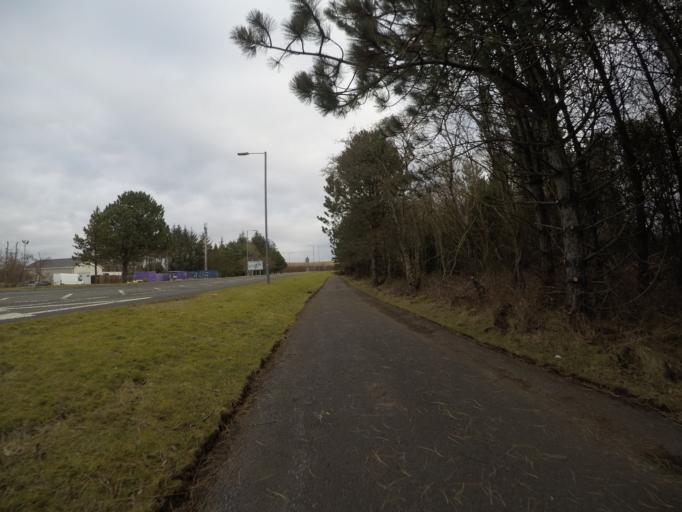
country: GB
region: Scotland
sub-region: North Ayrshire
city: Irvine
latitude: 55.5929
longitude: -4.6556
